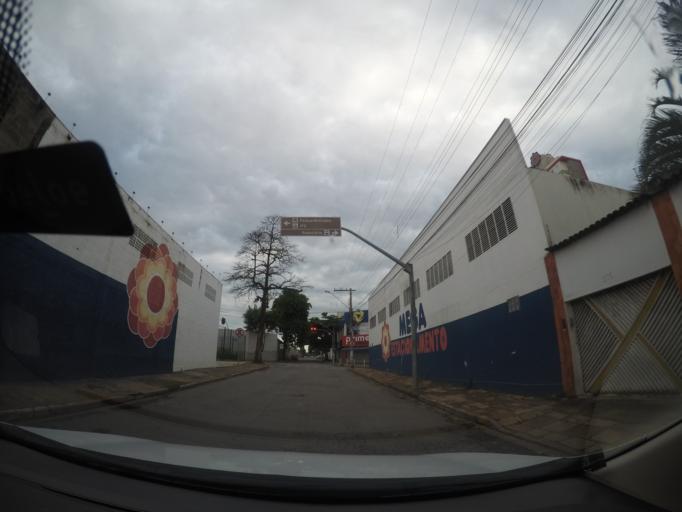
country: BR
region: Goias
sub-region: Goiania
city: Goiania
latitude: -16.6609
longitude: -49.2544
